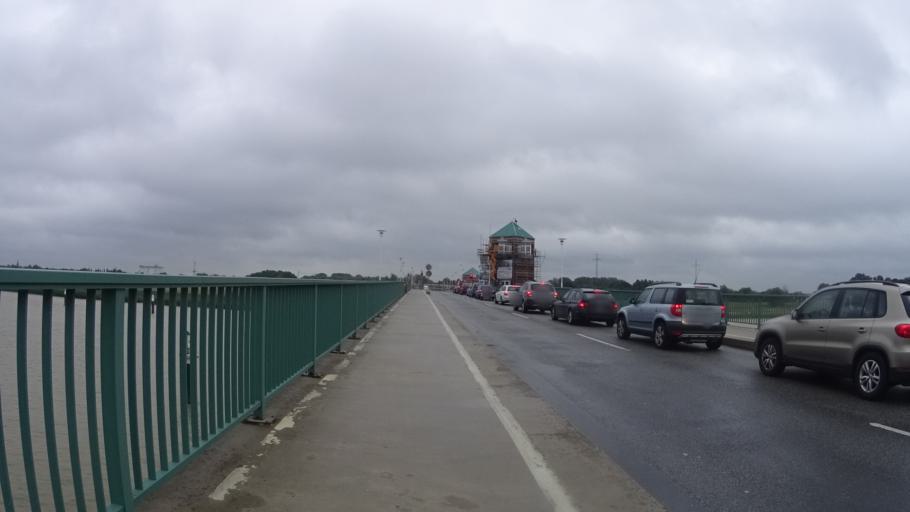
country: DE
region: Lower Saxony
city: Leer
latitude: 53.2184
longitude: 7.4246
